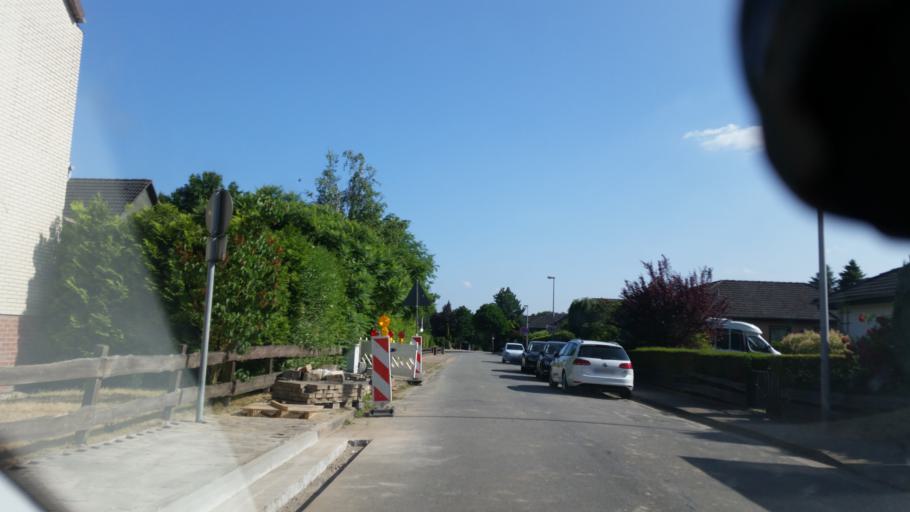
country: DE
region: Lower Saxony
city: Lehre
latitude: 52.3926
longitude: 10.6974
